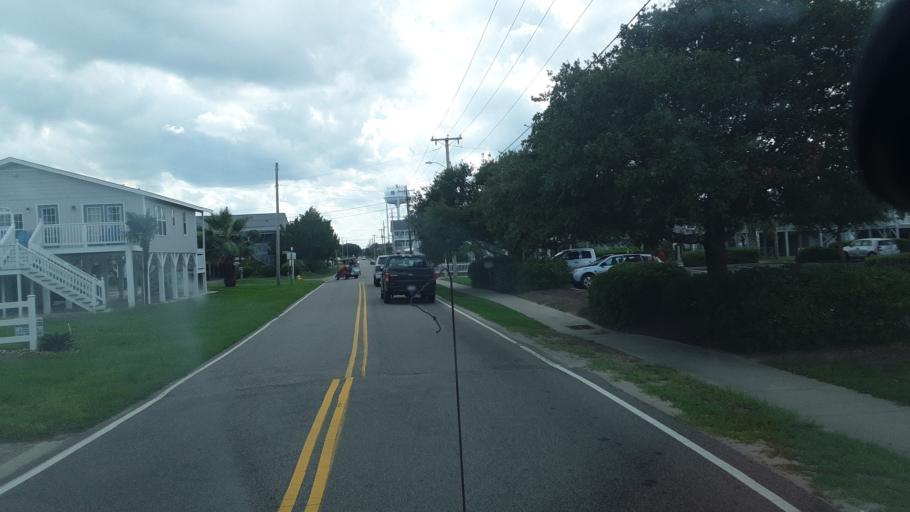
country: US
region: South Carolina
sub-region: Horry County
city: Little River
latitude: 33.8338
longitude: -78.6324
